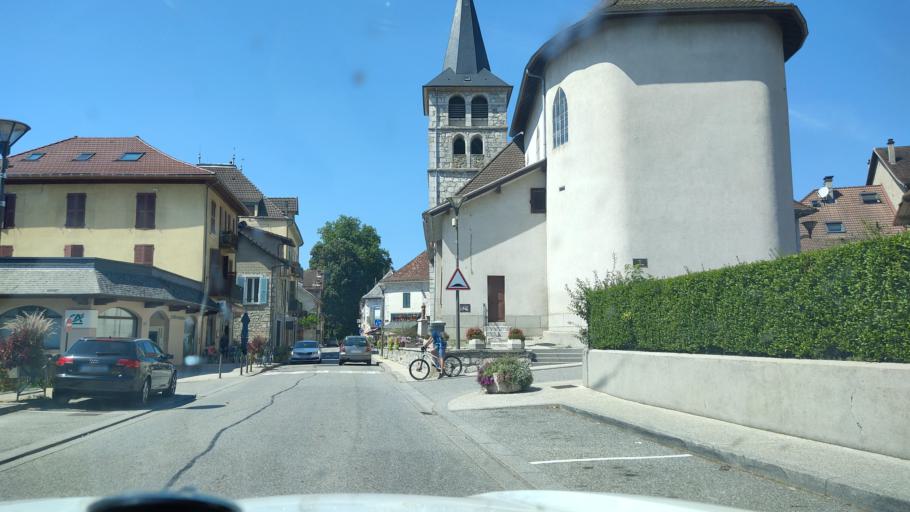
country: FR
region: Rhone-Alpes
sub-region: Departement de la Savoie
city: Novalaise
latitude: 45.5949
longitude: 5.7717
